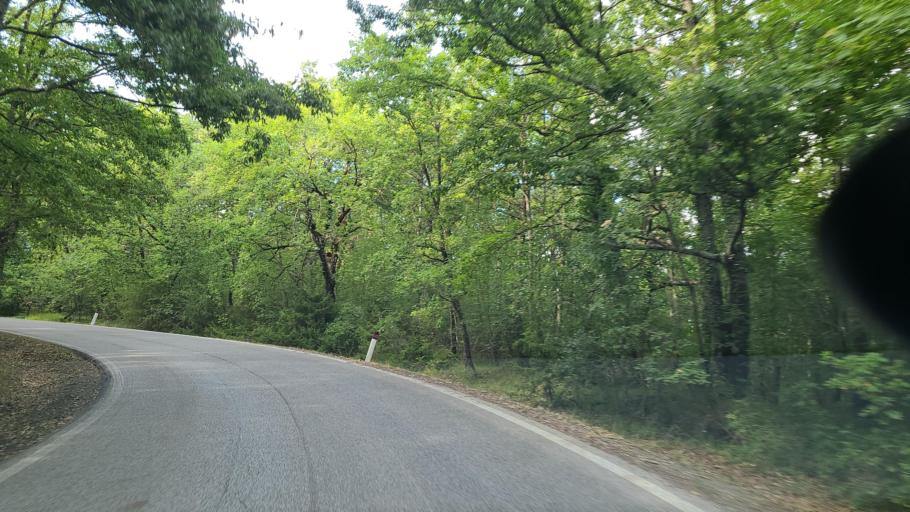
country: IT
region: Tuscany
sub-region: Provincia di Siena
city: San Gimignano
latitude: 43.4320
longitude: 10.9686
